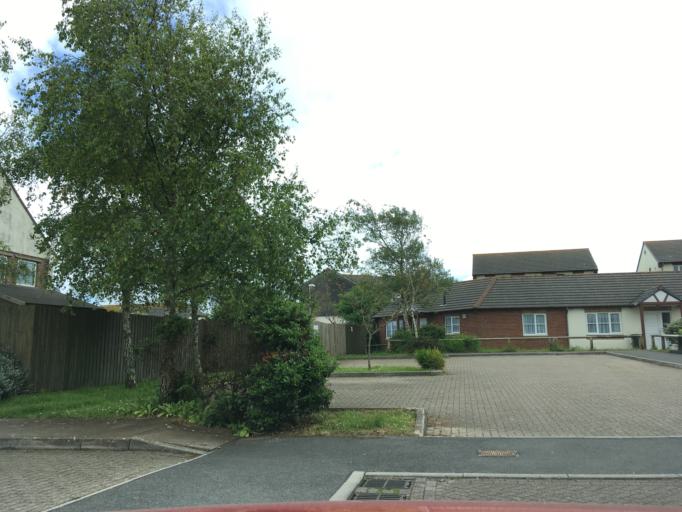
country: GB
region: England
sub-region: Devon
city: Dartmouth
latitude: 50.3493
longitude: -3.5997
